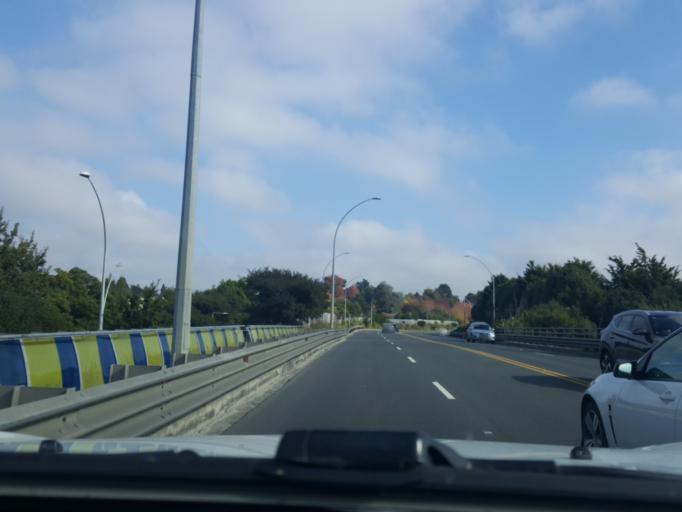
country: NZ
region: Waikato
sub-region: Hamilton City
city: Hamilton
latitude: -37.7429
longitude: 175.2544
